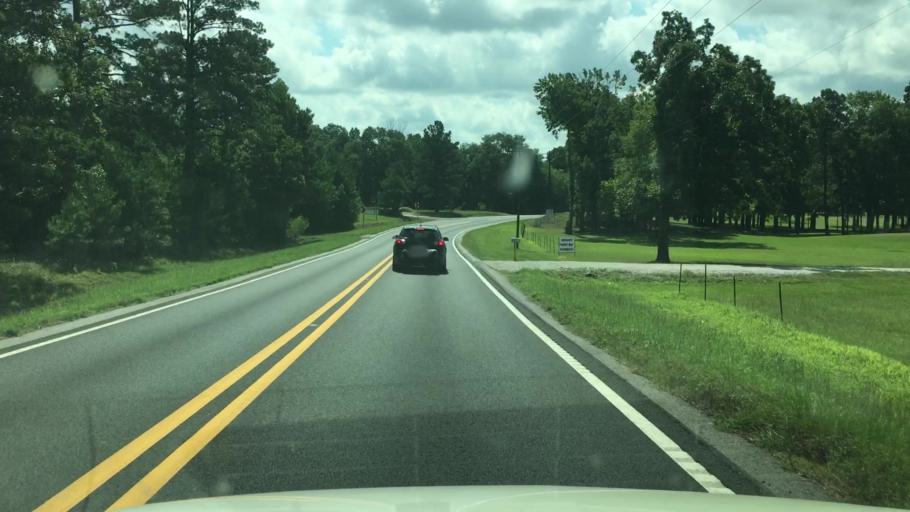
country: US
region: Arkansas
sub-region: Clark County
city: Arkadelphia
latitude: 34.2546
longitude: -93.1257
